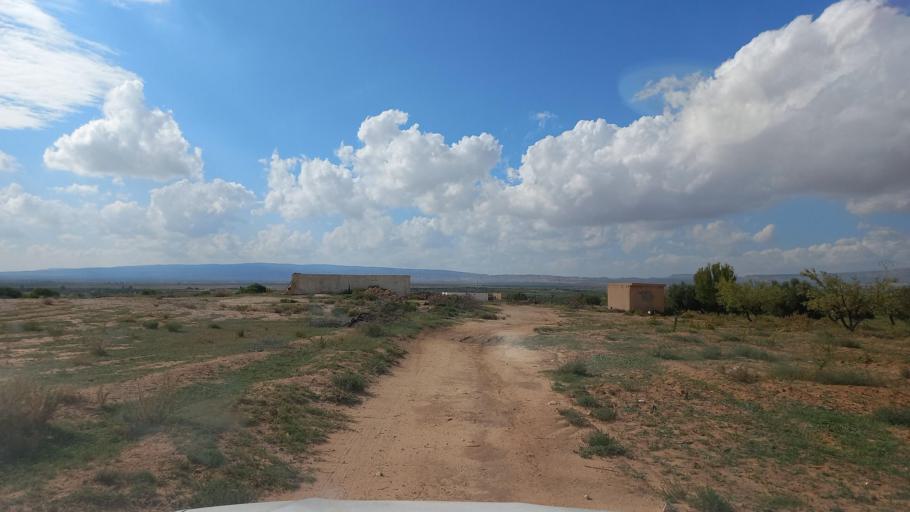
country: TN
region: Al Qasrayn
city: Sbiba
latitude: 35.3049
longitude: 9.1101
